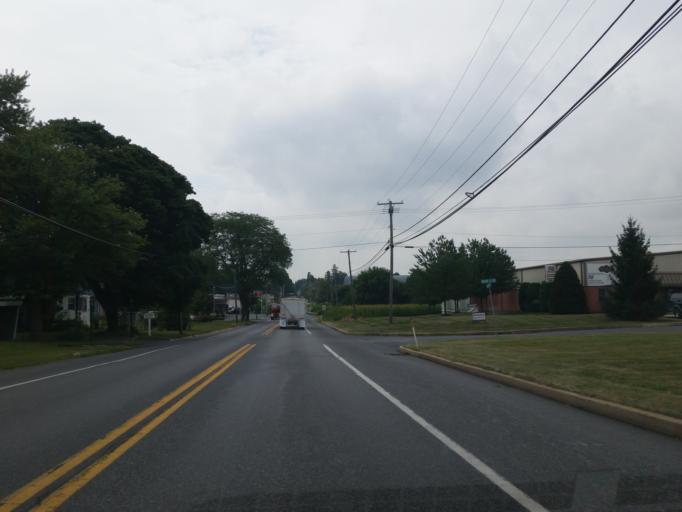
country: US
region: Pennsylvania
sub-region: Lancaster County
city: Lititz
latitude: 40.1704
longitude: -76.3083
